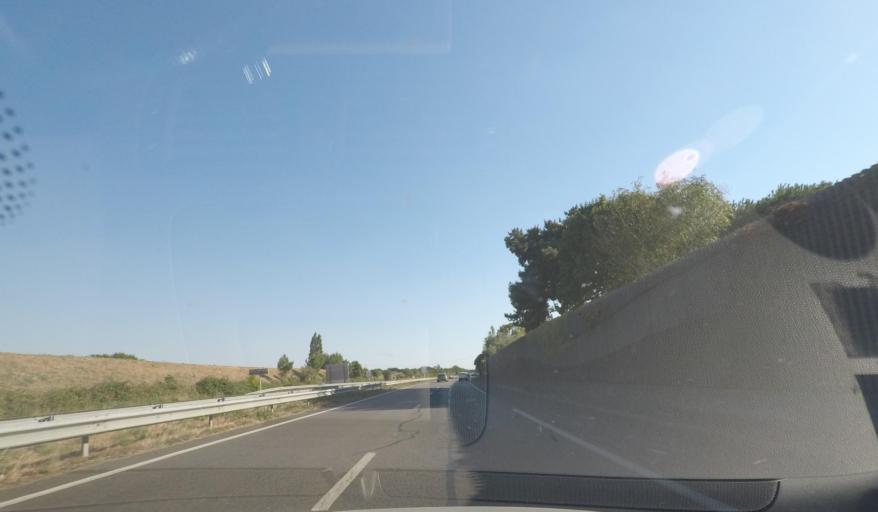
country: FR
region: Pays de la Loire
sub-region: Departement de la Loire-Atlantique
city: Saint-Brevin-les-Pins
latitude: 47.2565
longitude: -2.1585
